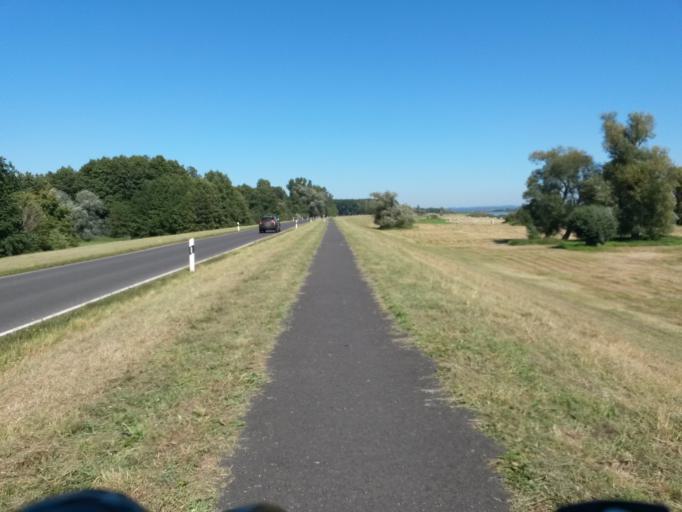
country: DE
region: Brandenburg
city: Oderberg
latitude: 52.8516
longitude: 14.1255
